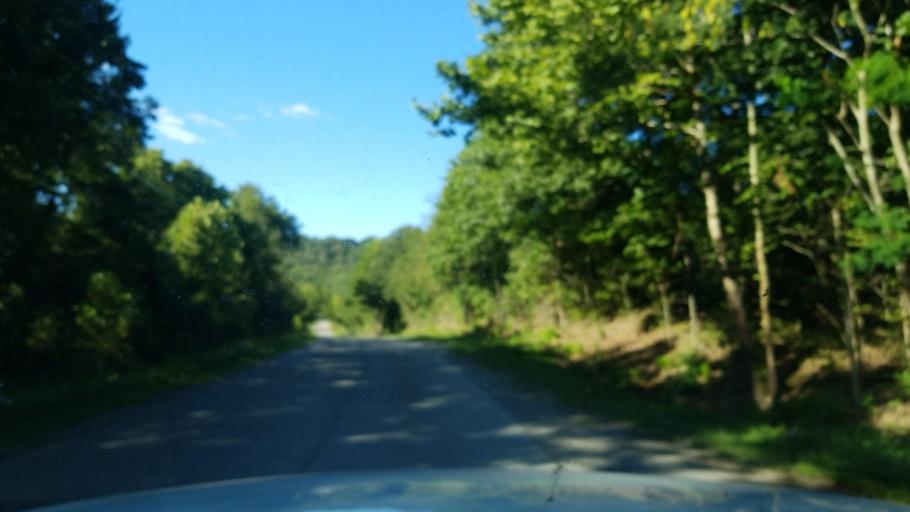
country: US
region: Illinois
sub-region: Hardin County
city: Elizabethtown
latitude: 37.5922
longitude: -88.3653
